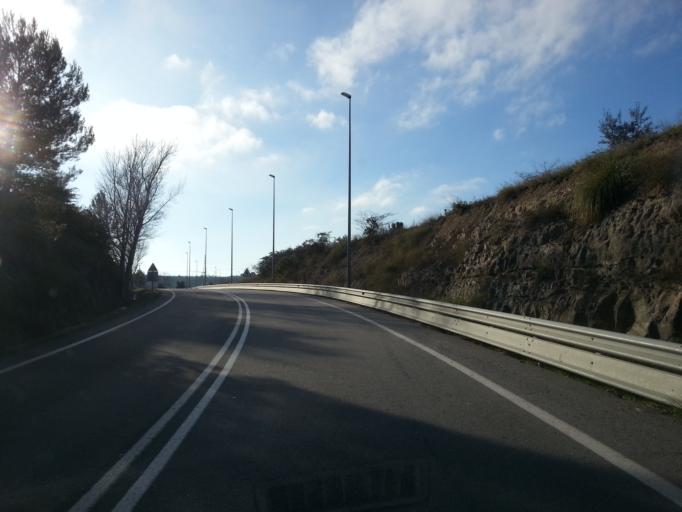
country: ES
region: Catalonia
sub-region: Provincia de Barcelona
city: Sant Fruitos de Bages
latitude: 41.7280
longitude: 1.8634
